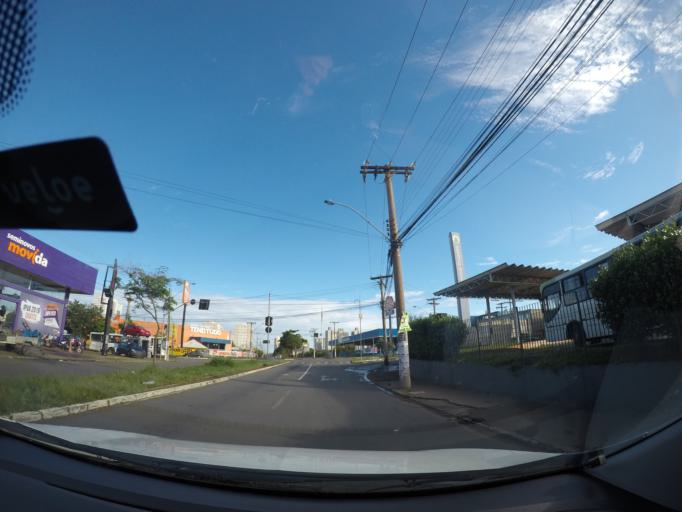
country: BR
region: Goias
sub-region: Goiania
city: Goiania
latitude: -16.7455
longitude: -49.2820
